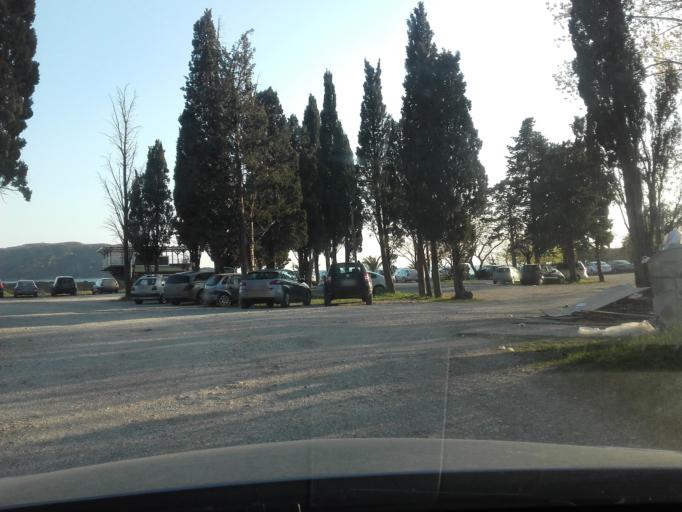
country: ME
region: Budva
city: Budva
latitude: 42.2860
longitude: 18.8516
